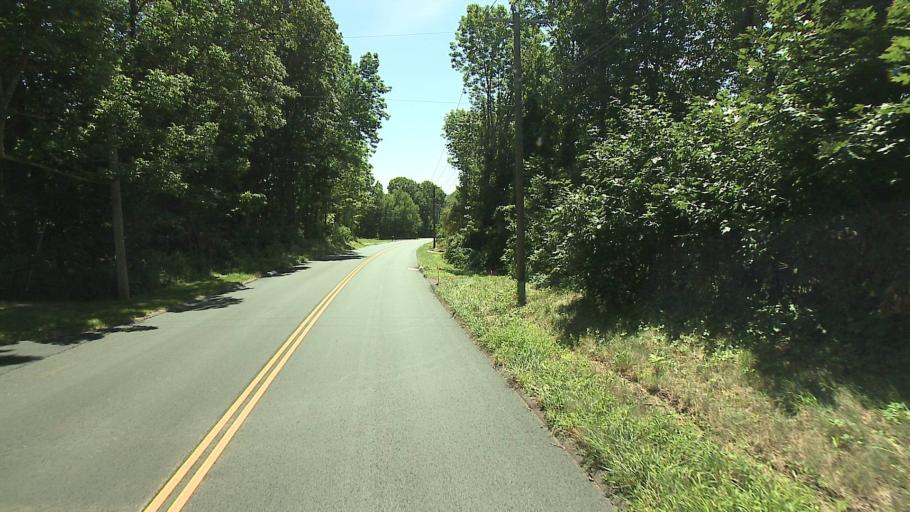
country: US
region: Connecticut
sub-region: Hartford County
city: West Simsbury
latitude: 41.9243
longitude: -72.9091
